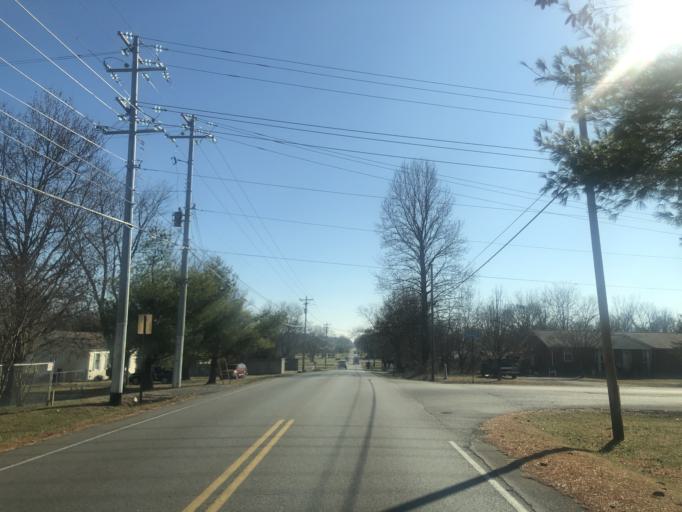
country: US
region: Tennessee
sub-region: Rutherford County
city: Smyrna
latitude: 35.9313
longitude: -86.4895
